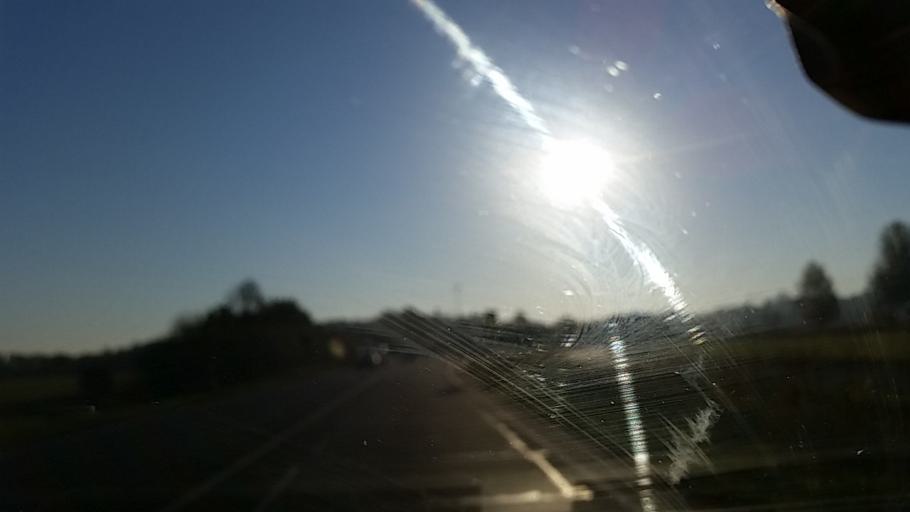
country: DE
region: Lower Saxony
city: Wolfsburg
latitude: 52.4266
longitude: 10.8282
